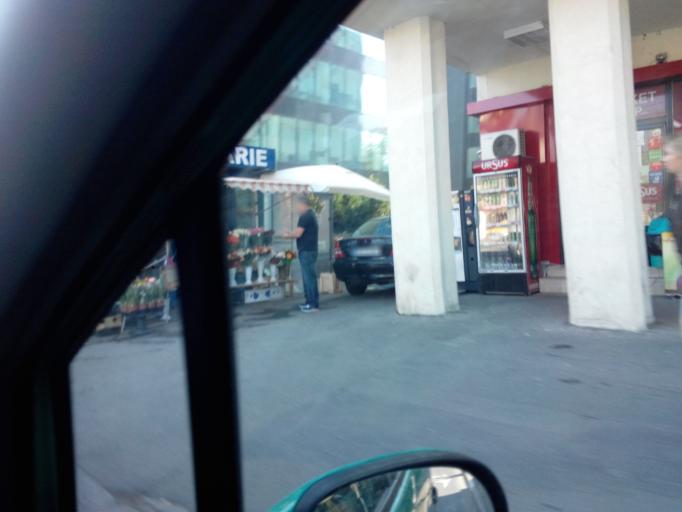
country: RO
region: Bucuresti
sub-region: Municipiul Bucuresti
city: Bucharest
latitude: 44.4566
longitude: 26.1060
